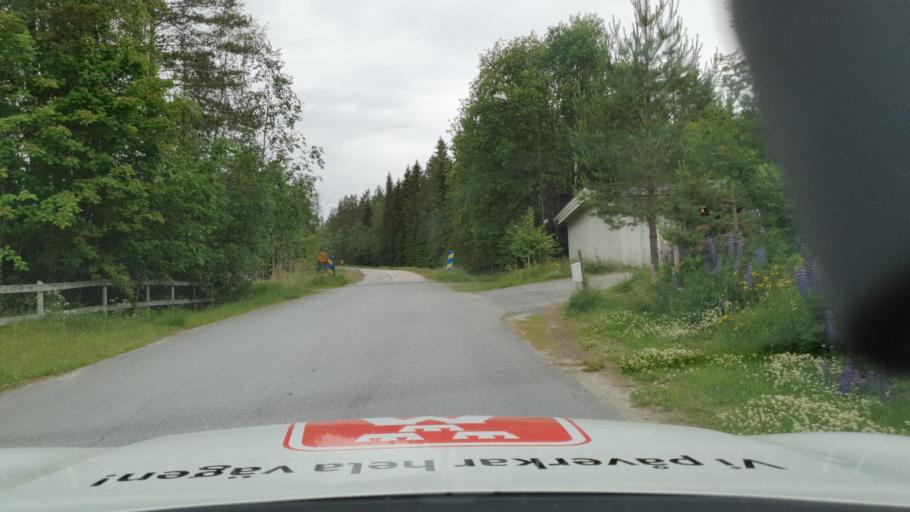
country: SE
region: Vaesterbotten
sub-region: Nordmalings Kommun
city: Nordmaling
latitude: 63.5313
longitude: 19.4341
